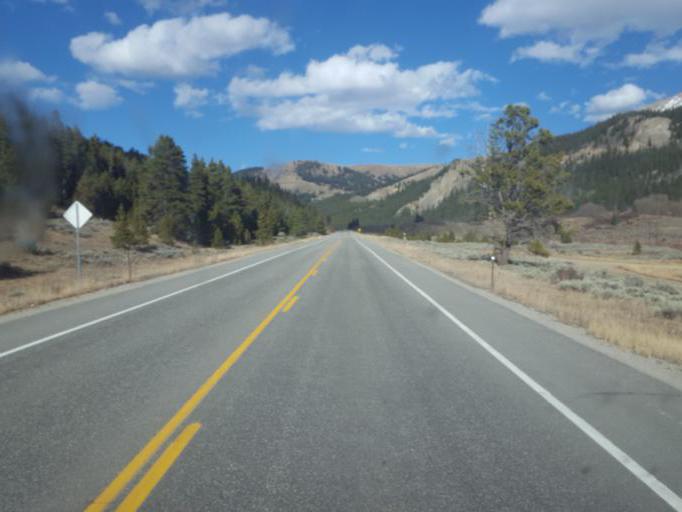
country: US
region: Colorado
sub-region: Lake County
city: Leadville
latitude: 39.3138
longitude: -106.2264
